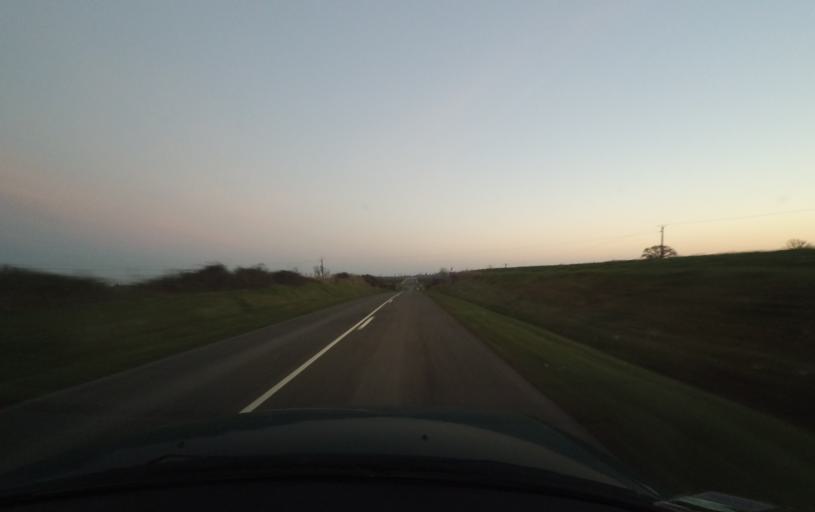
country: FR
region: Pays de la Loire
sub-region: Departement de la Mayenne
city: Soulge-sur-Ouette
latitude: 48.0381
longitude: -0.5753
